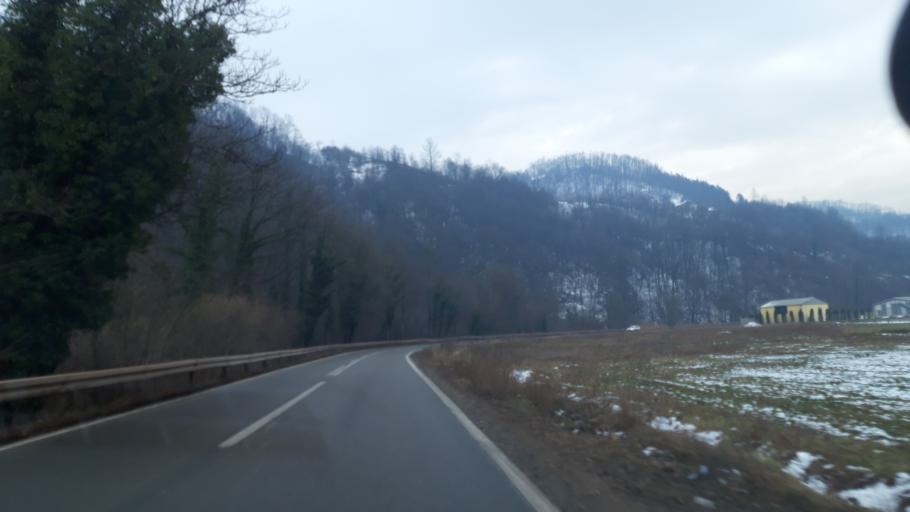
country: BA
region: Republika Srpska
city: Milici
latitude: 44.1870
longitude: 19.0753
